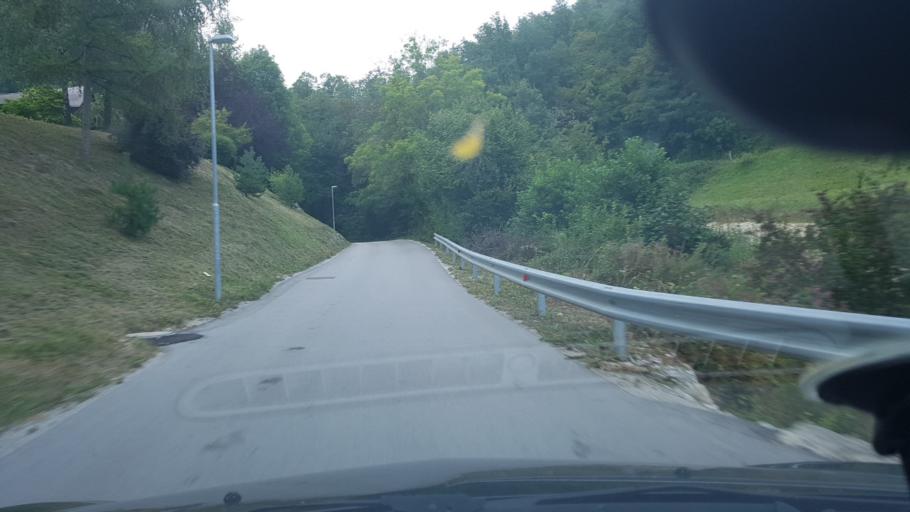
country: SI
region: Krsko
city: Senovo
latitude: 46.0130
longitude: 15.4890
